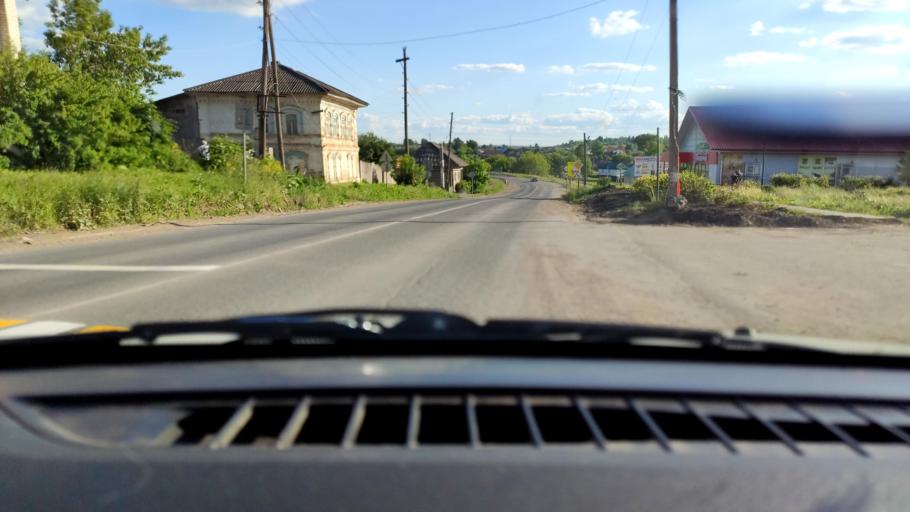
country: RU
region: Perm
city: Orda
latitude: 57.1959
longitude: 56.9060
